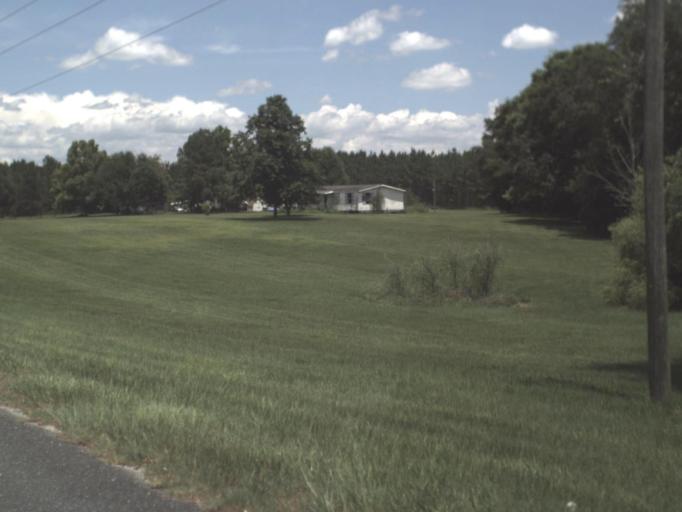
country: US
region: Florida
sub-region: Suwannee County
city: Wellborn
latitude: 30.0676
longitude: -82.7825
